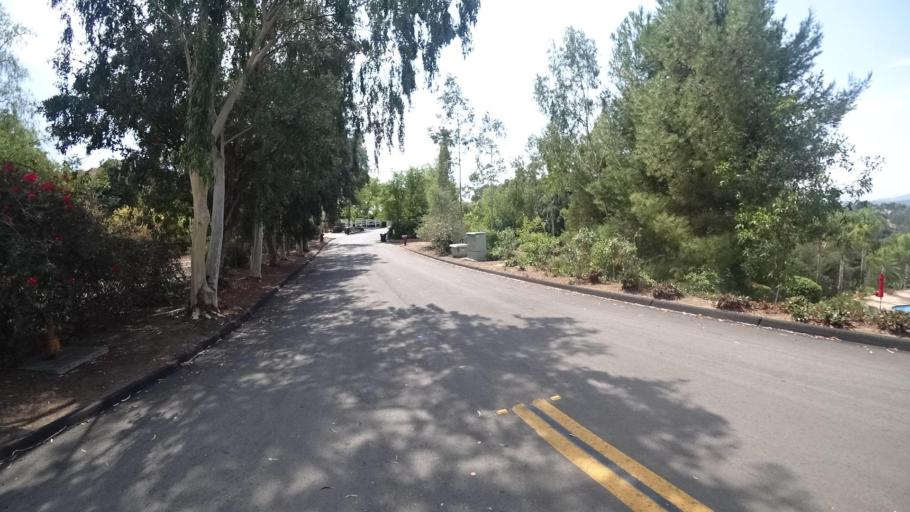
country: US
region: California
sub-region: San Diego County
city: Escondido
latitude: 33.0995
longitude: -117.0454
